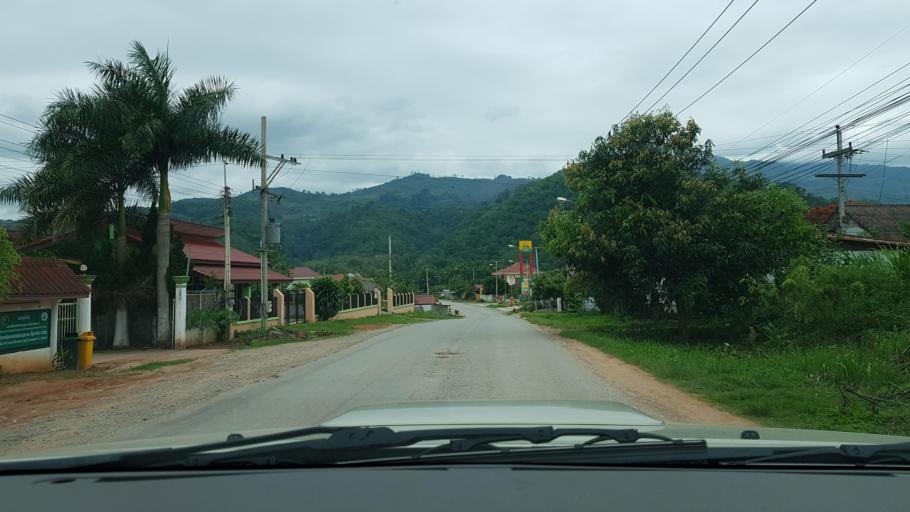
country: LA
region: Oudomxai
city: Muang Xay
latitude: 20.6986
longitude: 101.9998
